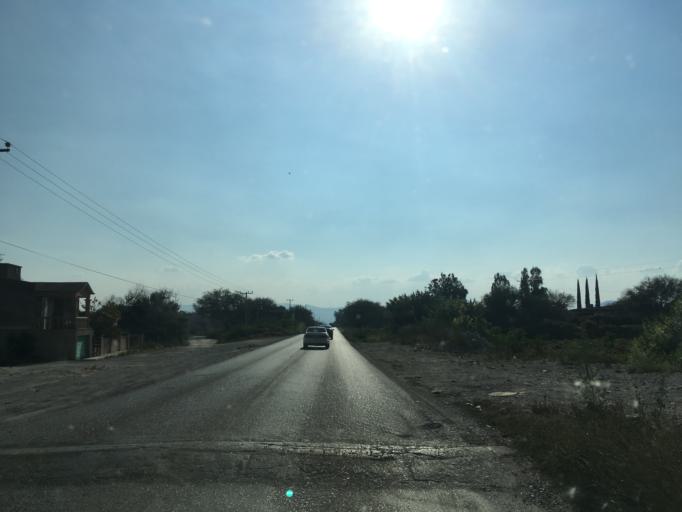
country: MX
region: Hidalgo
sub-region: Ixmiquilpan
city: El Nith
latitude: 20.5515
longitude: -99.1640
